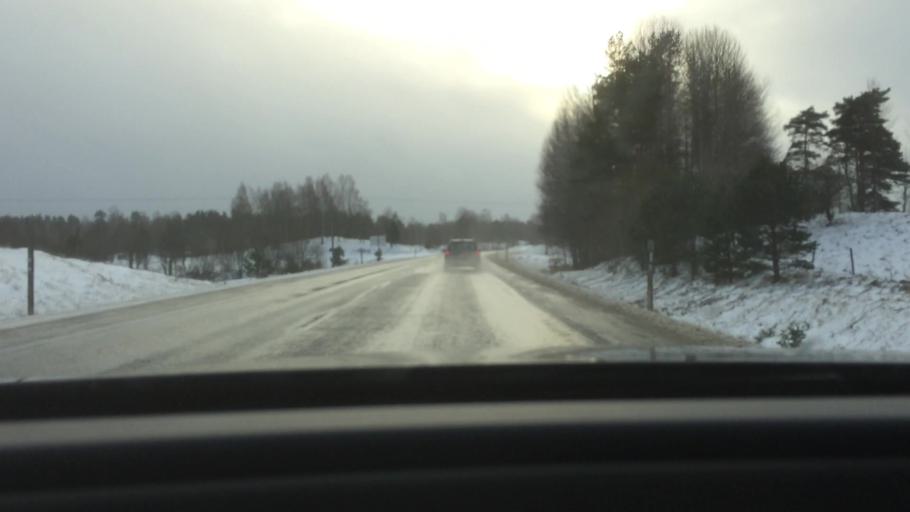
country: SE
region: Vaestra Goetaland
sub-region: Falkopings Kommun
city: Falkoeping
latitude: 57.9724
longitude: 13.5296
